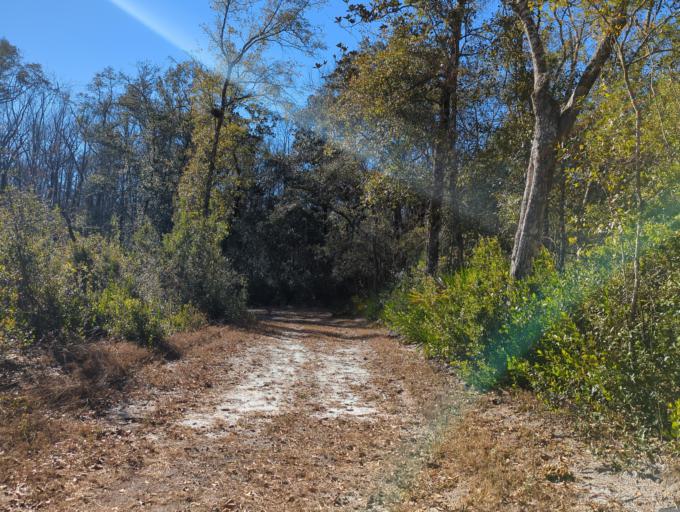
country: US
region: Florida
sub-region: Wakulla County
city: Crawfordville
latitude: 30.1849
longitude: -84.3306
